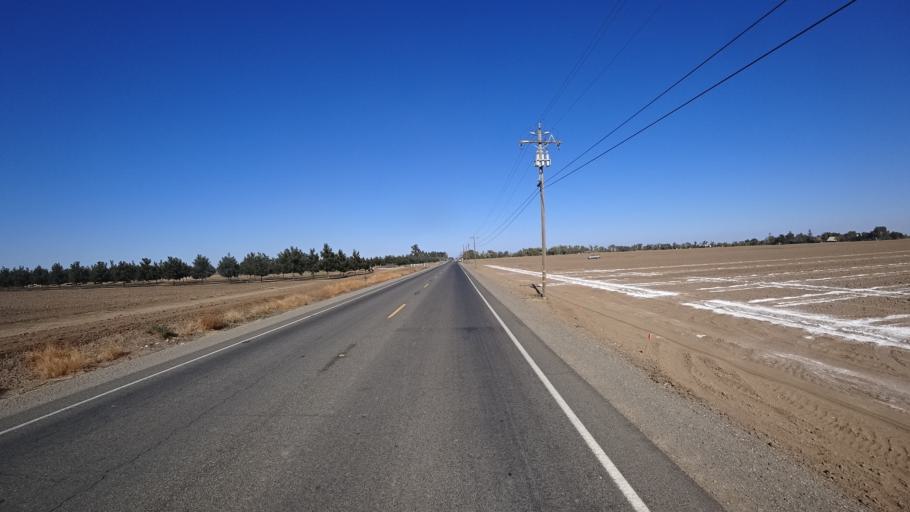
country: US
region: California
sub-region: Yolo County
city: Davis
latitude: 38.5838
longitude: -121.8032
